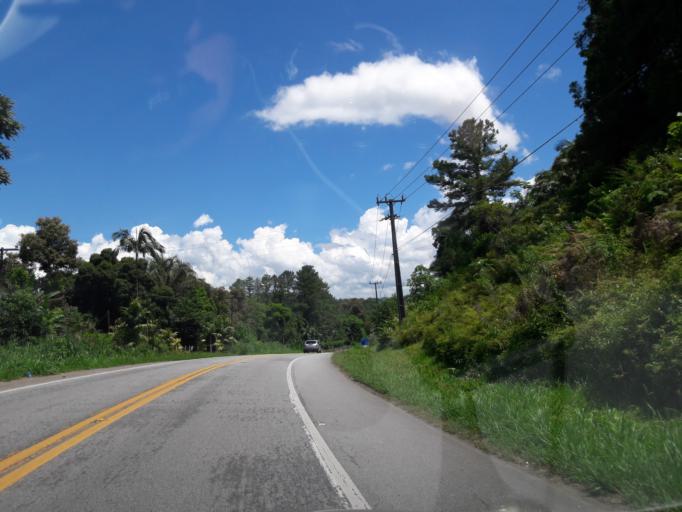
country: BR
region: Parana
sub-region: Antonina
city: Antonina
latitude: -25.4550
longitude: -48.8077
